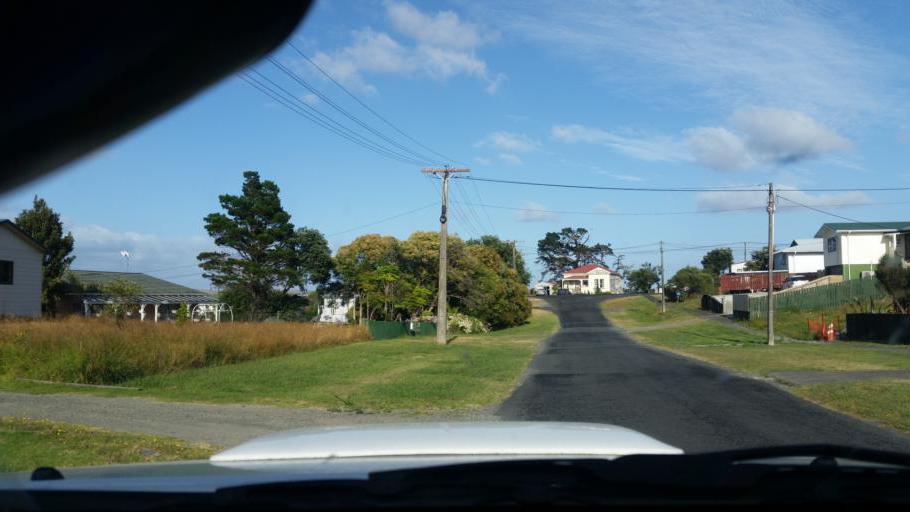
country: NZ
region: Northland
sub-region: Kaipara District
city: Dargaville
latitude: -35.9365
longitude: 173.8598
